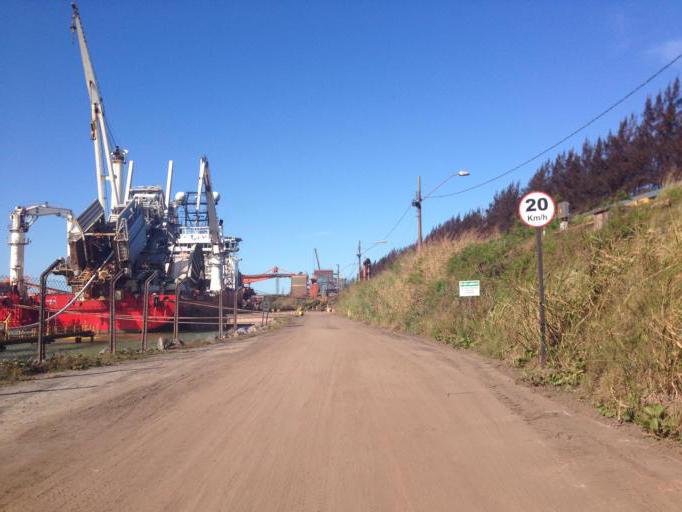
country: BR
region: Espirito Santo
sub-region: Guarapari
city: Guarapari
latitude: -20.7880
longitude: -40.5753
